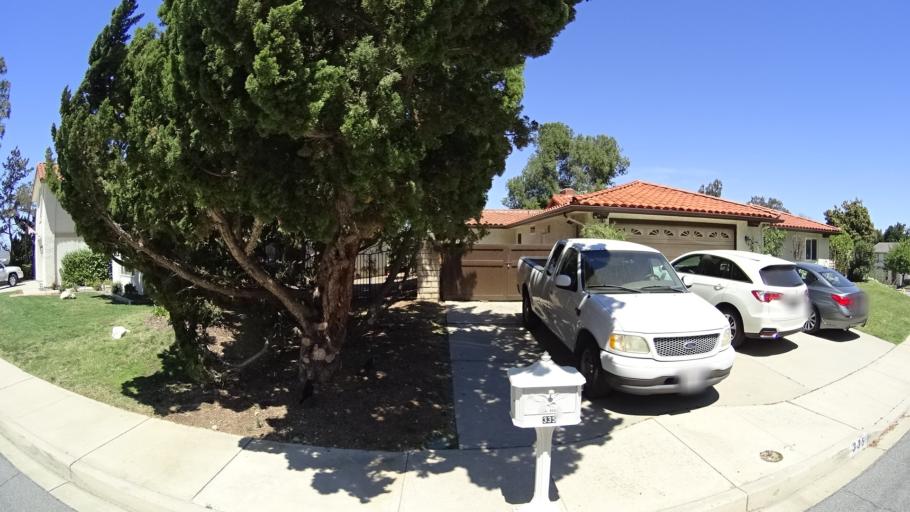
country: US
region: California
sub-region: Ventura County
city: Casa Conejo
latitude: 34.1731
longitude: -118.8988
